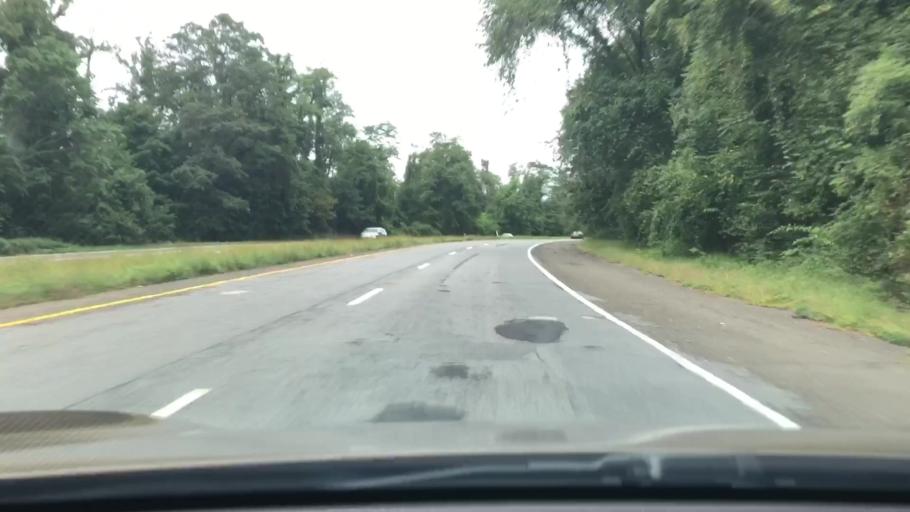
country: US
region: New York
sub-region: Westchester County
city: Briarcliff Manor
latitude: 41.1193
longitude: -73.8253
